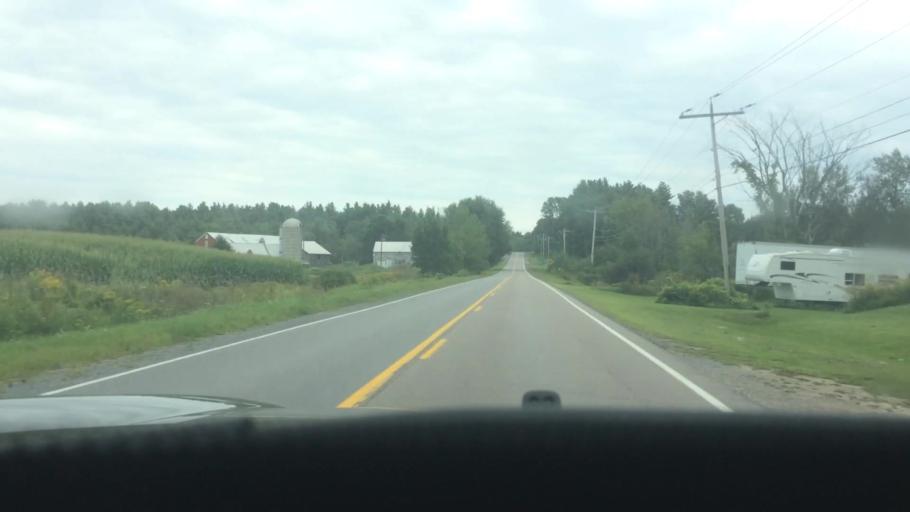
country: US
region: New York
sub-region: St. Lawrence County
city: Hannawa Falls
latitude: 44.5378
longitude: -75.0227
